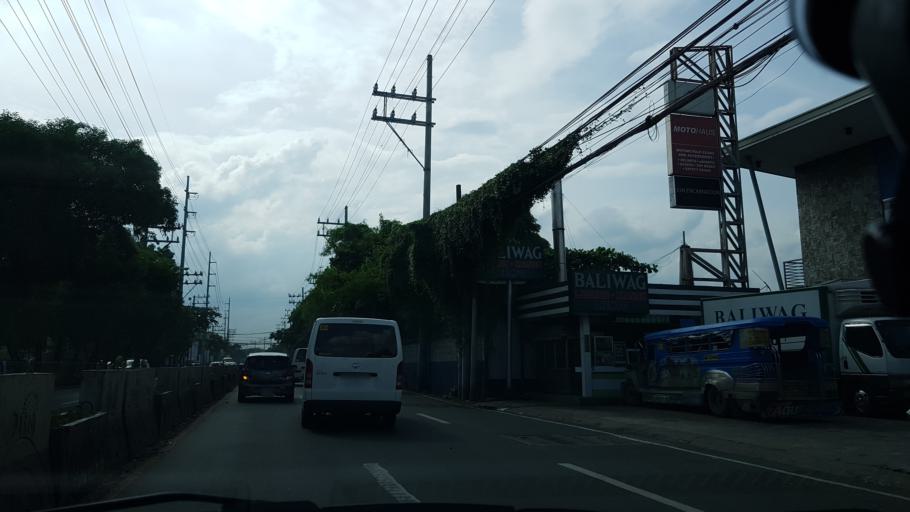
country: PH
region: Calabarzon
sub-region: Province of Rizal
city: Cainta
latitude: 14.5886
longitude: 121.1051
